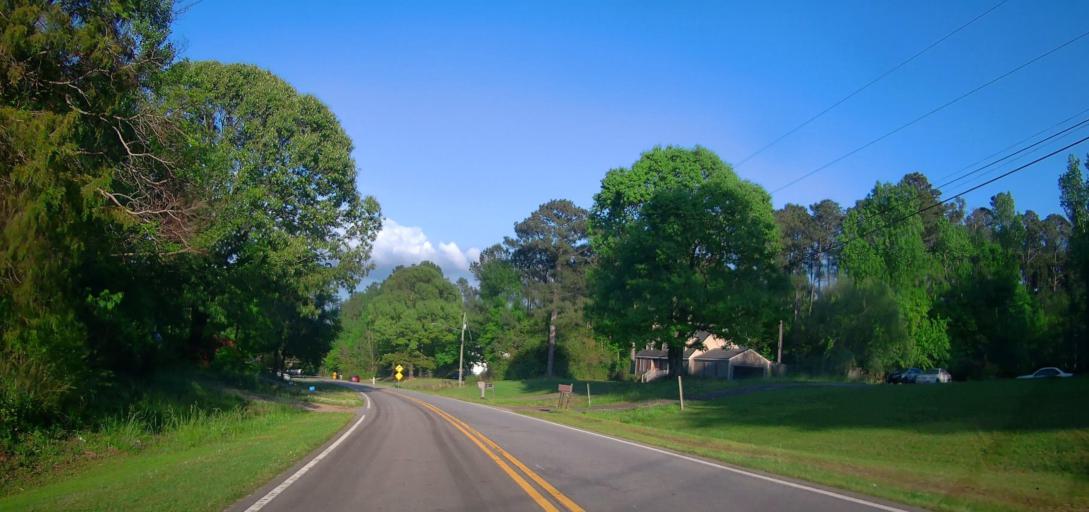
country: US
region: Georgia
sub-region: Putnam County
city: Eatonton
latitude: 33.3160
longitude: -83.3701
